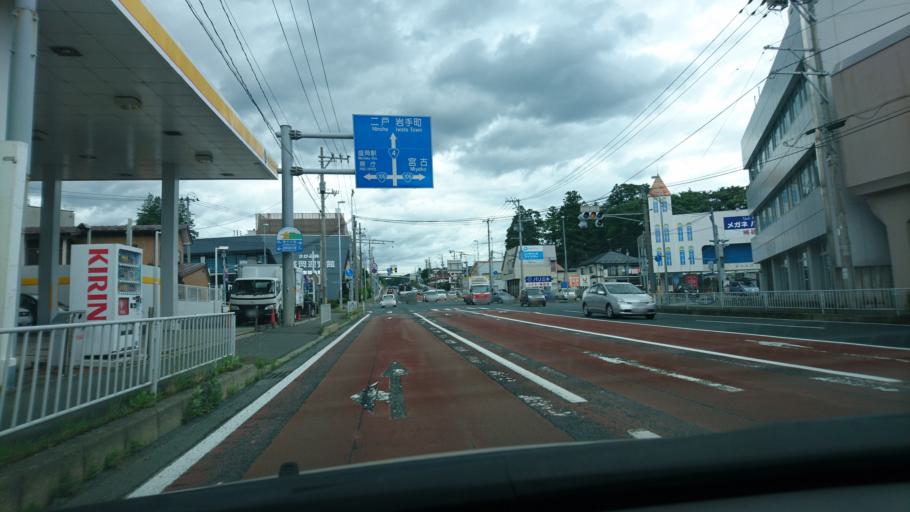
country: JP
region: Iwate
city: Morioka-shi
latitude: 39.6947
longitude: 141.1670
